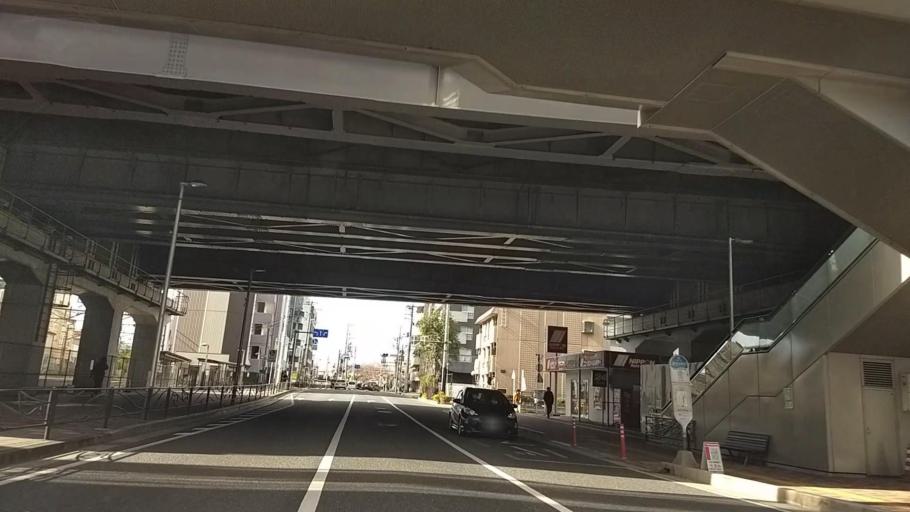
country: JP
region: Tokyo
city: Chofugaoka
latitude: 35.6212
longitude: 139.5699
